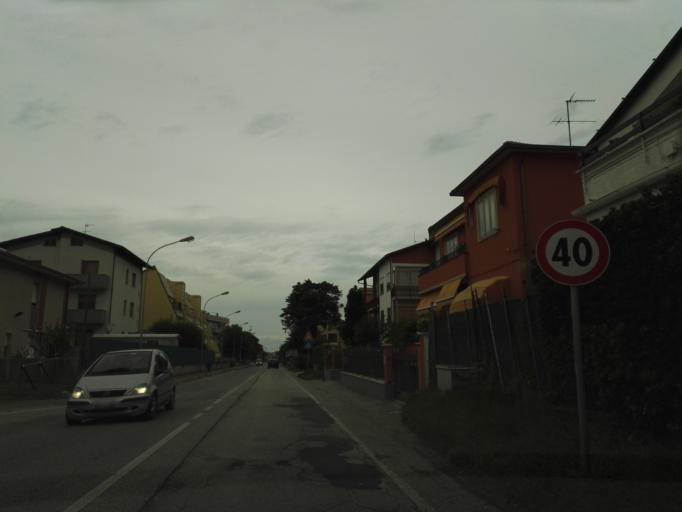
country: IT
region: The Marches
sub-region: Provincia di Pesaro e Urbino
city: Marotta
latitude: 43.7635
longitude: 13.1379
